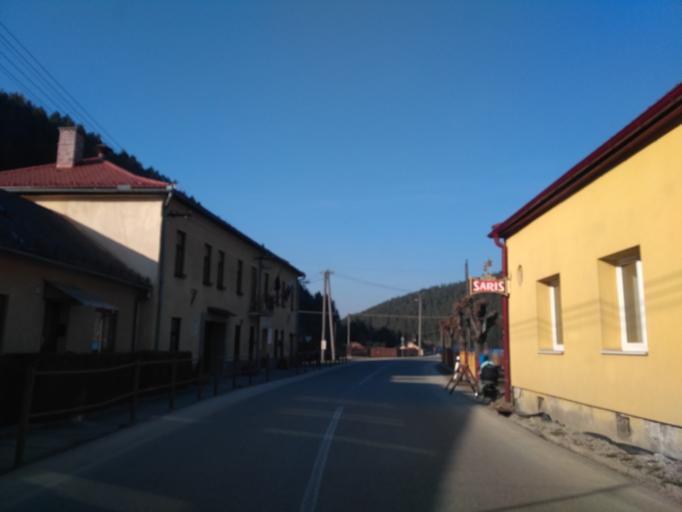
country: SK
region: Kosicky
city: Medzev
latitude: 48.7457
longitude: 20.7740
